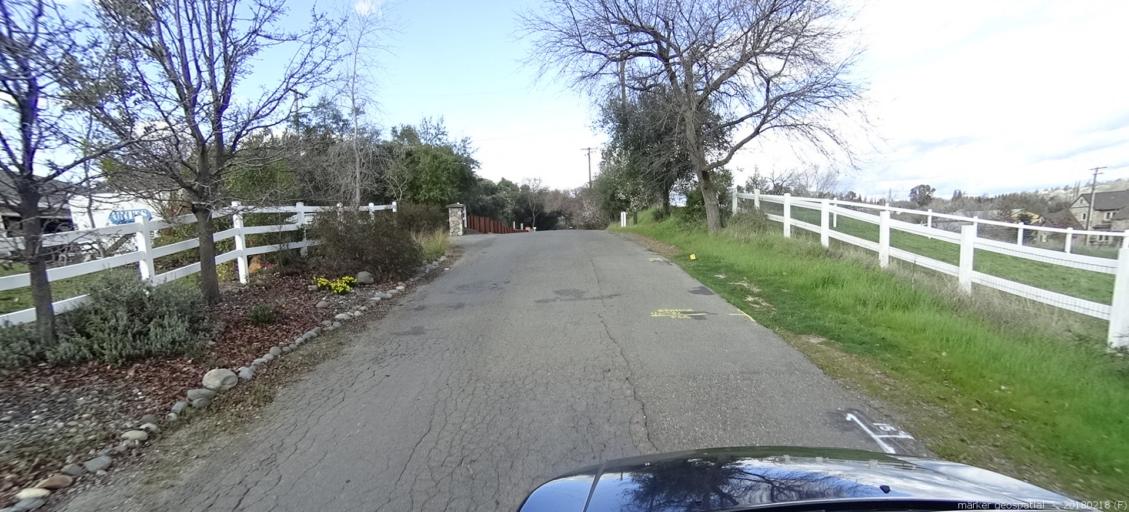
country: US
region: California
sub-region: Sacramento County
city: Orangevale
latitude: 38.7024
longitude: -121.2065
